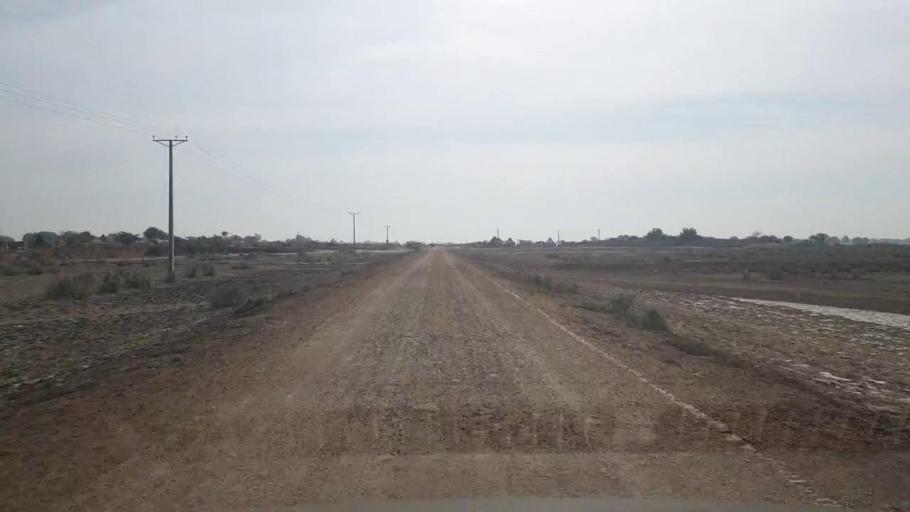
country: PK
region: Sindh
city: Umarkot
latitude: 25.3603
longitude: 69.6514
